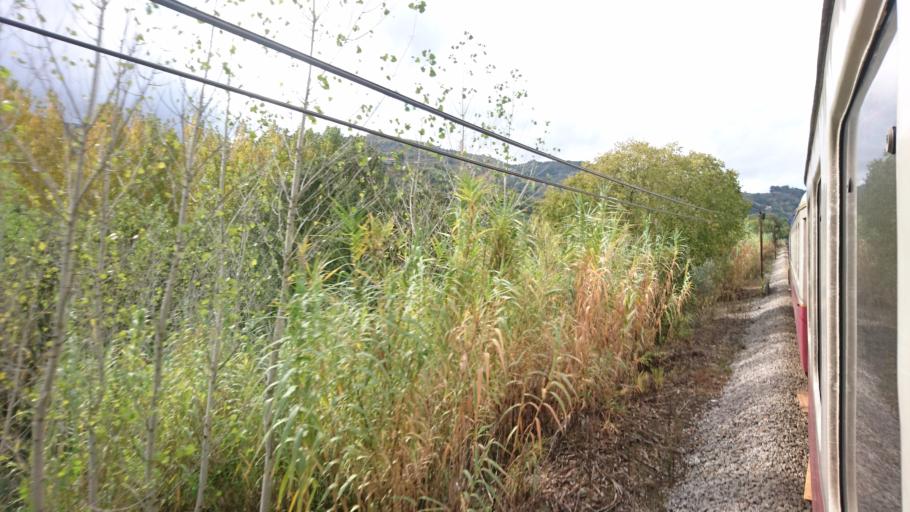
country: PT
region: Vila Real
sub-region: Mesao Frio
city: Mesao Frio
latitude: 41.1220
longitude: -7.9121
